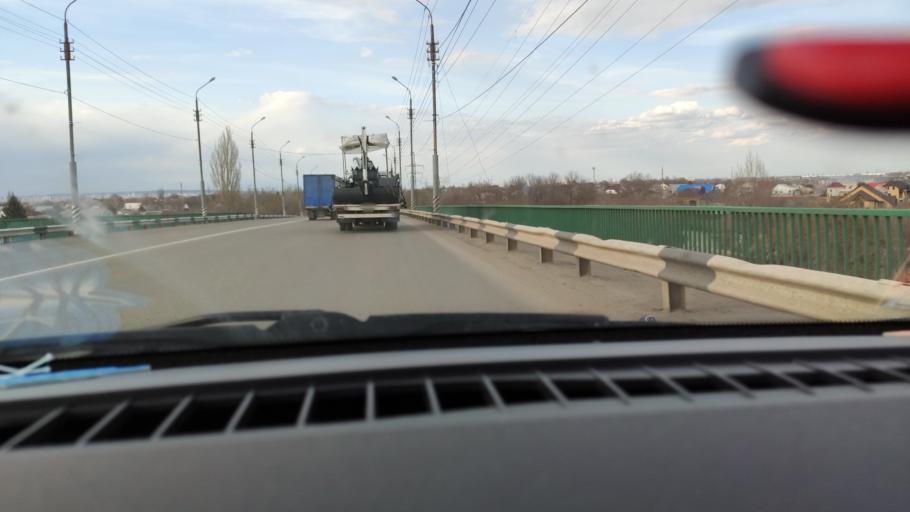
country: RU
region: Saratov
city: Privolzhskiy
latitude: 51.4192
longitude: 46.0463
